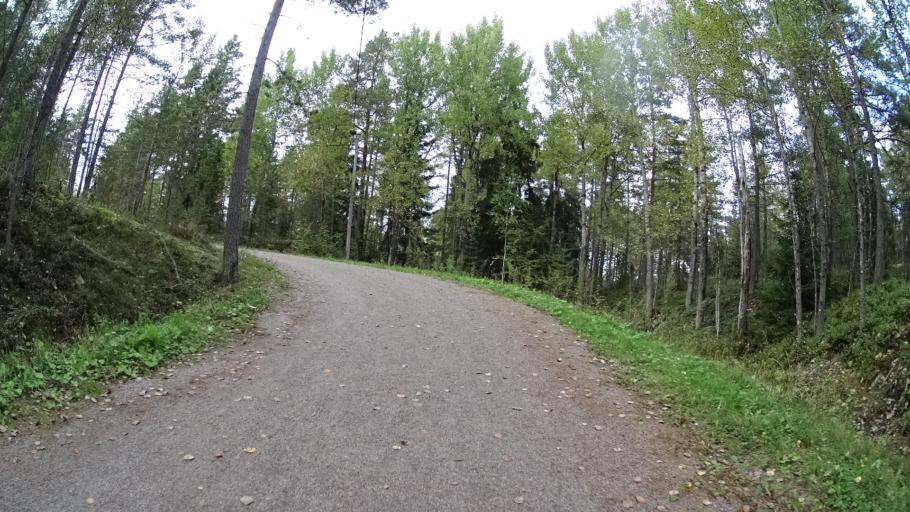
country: FI
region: Uusimaa
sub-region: Helsinki
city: Kauniainen
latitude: 60.1958
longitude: 24.7046
